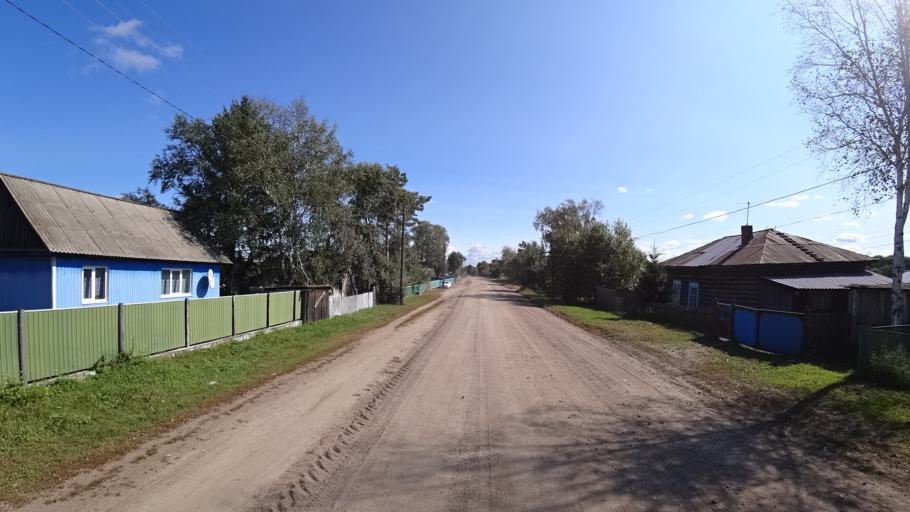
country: RU
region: Amur
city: Arkhara
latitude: 49.4026
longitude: 130.1423
